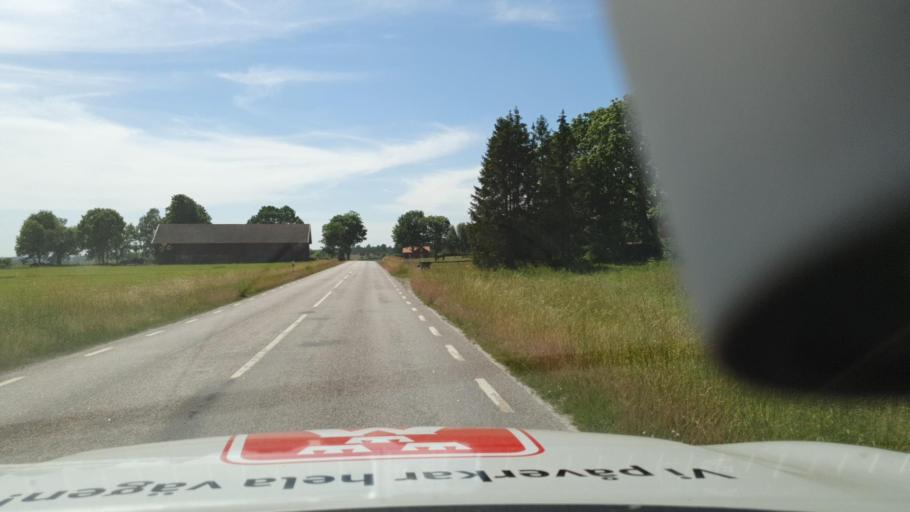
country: SE
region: Vaestra Goetaland
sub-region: Vara Kommun
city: Vara
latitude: 58.4813
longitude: 12.8967
